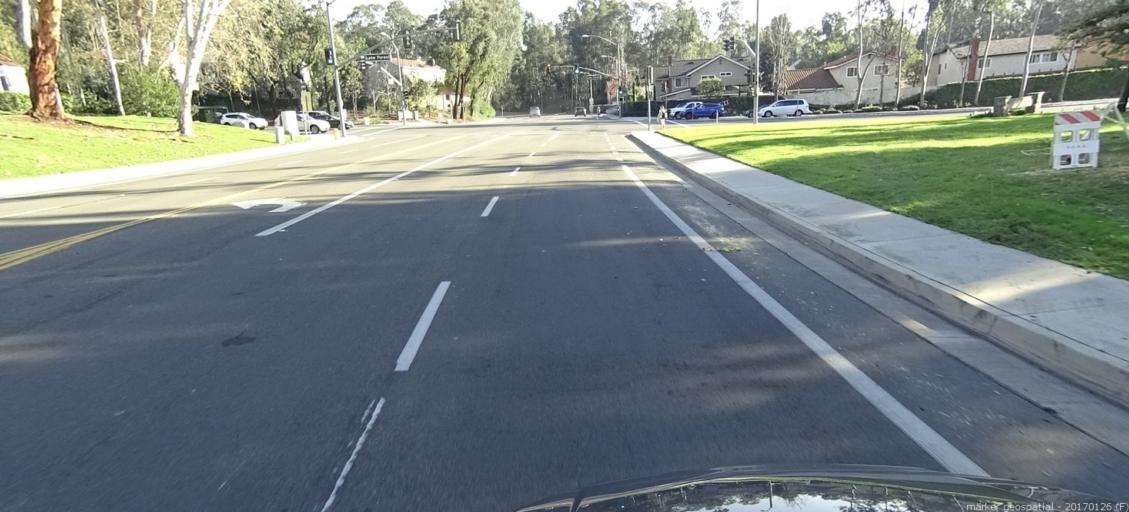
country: US
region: California
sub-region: Orange County
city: Lake Forest
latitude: 33.6428
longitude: -117.6980
